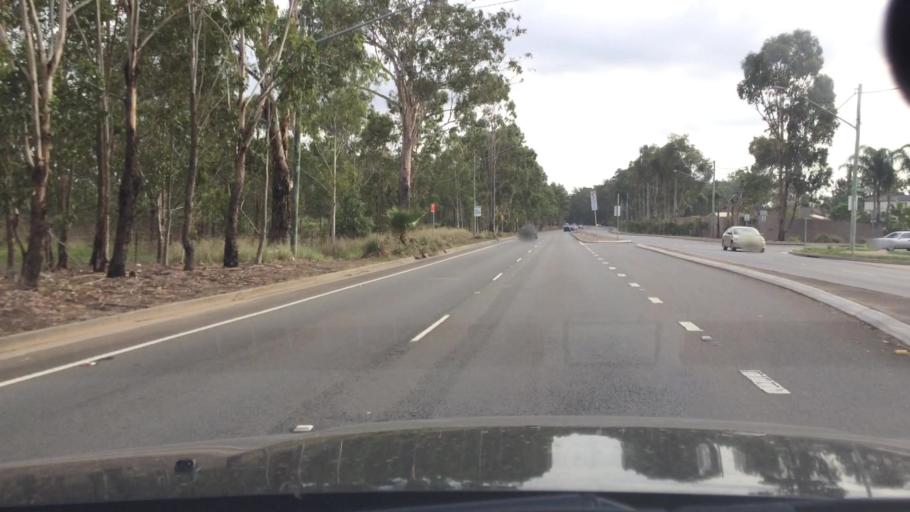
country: AU
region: New South Wales
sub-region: Fairfield
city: Horsley Park
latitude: -33.8589
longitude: 150.8732
